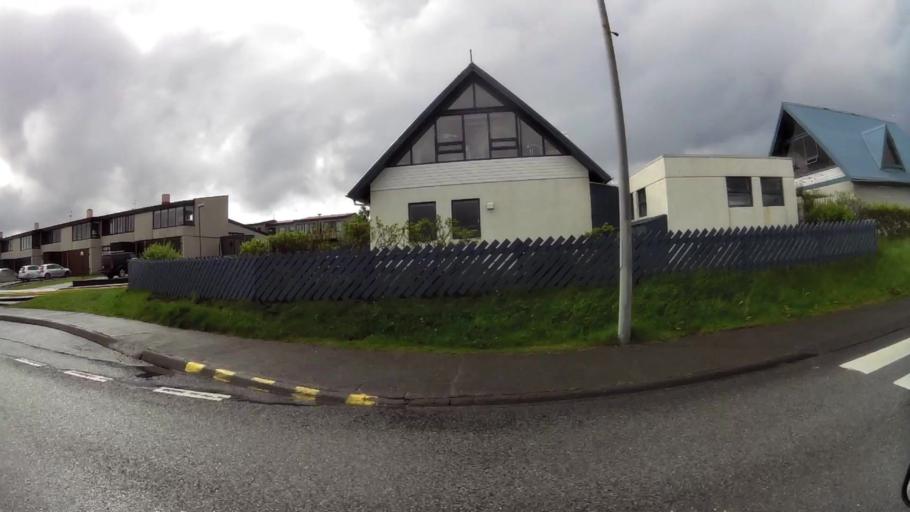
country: IS
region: Capital Region
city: Seltjarnarnes
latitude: 64.1578
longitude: -21.9932
